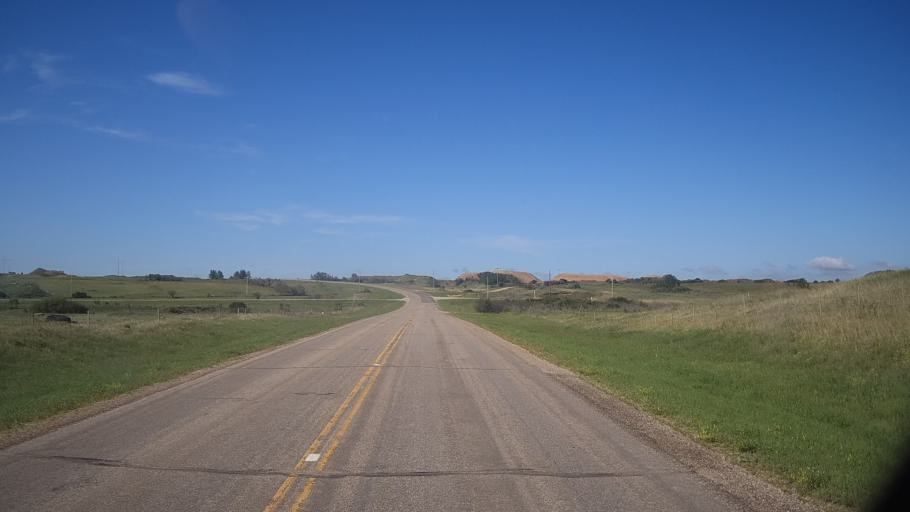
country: CA
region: Saskatchewan
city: Watrous
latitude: 51.7096
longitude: -105.3756
